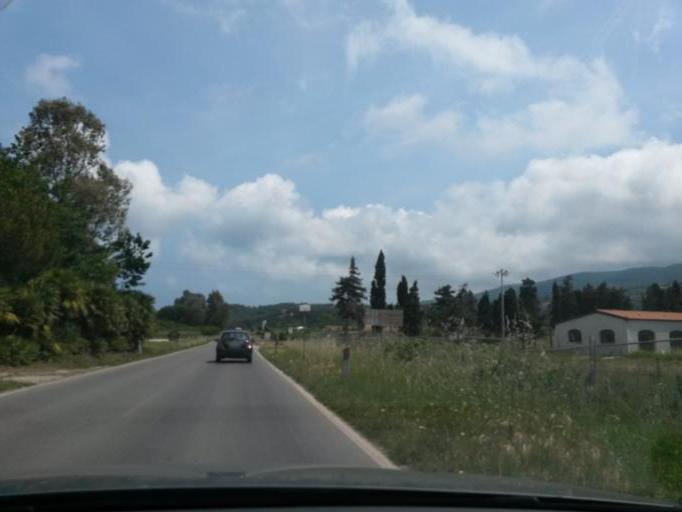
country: IT
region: Tuscany
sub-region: Provincia di Livorno
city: Capoliveri
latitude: 42.7597
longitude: 10.3717
